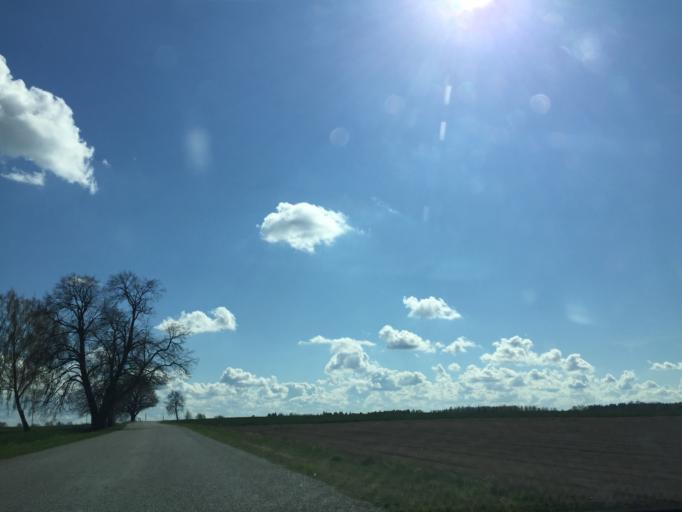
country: LV
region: Strenci
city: Strenci
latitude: 57.5192
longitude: 25.6811
